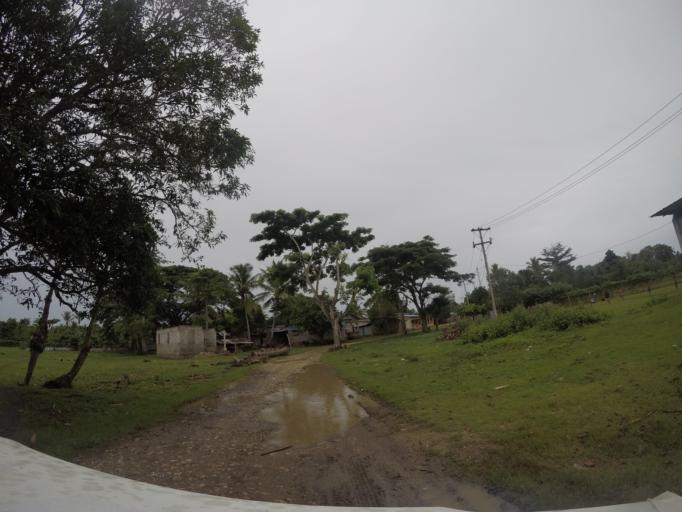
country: TL
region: Lautem
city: Lospalos
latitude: -8.5265
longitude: 127.0012
